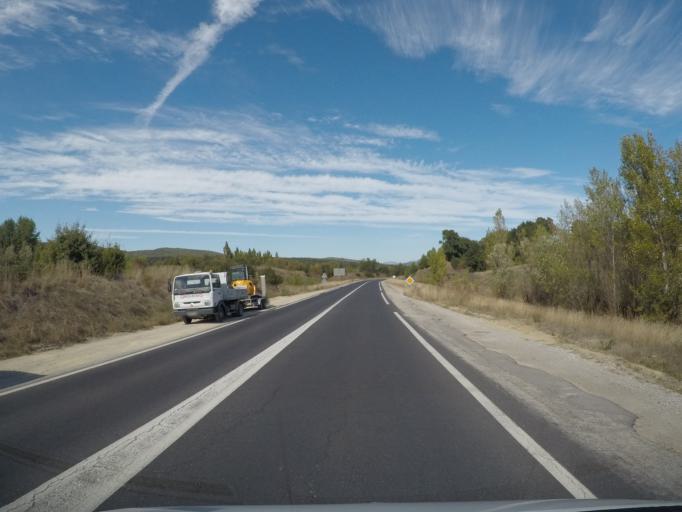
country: FR
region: Languedoc-Roussillon
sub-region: Departement de l'Herault
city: Saint-Martin-de-Londres
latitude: 43.7899
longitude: 3.7367
